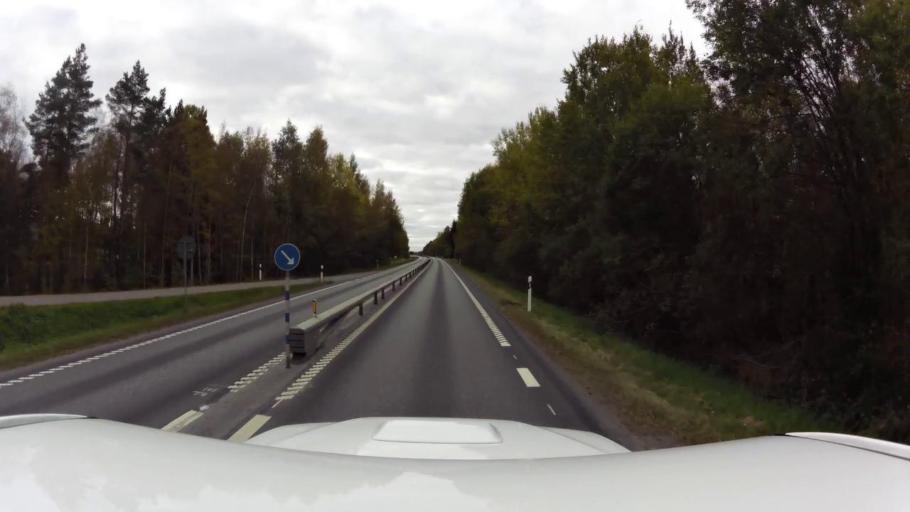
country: SE
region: OEstergoetland
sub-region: Linkopings Kommun
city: Malmslatt
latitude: 58.3825
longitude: 15.5422
